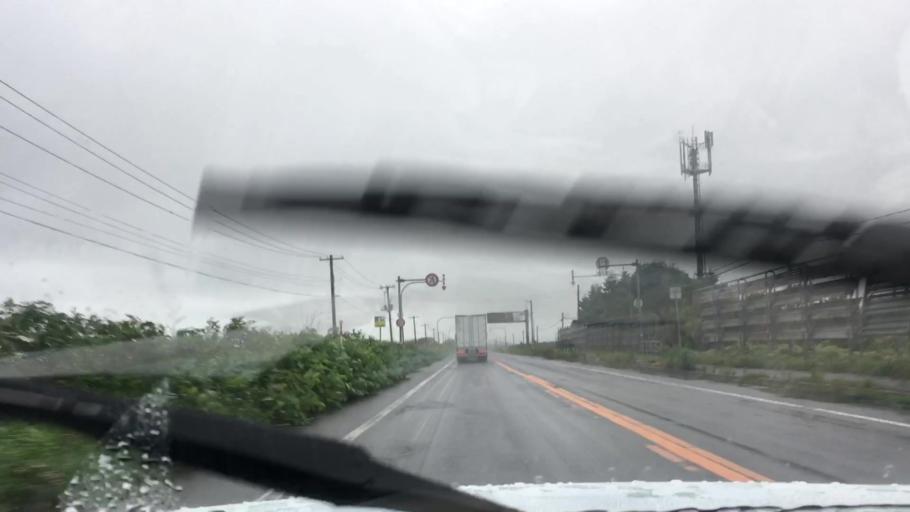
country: JP
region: Hokkaido
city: Niseko Town
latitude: 42.4315
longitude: 140.3186
